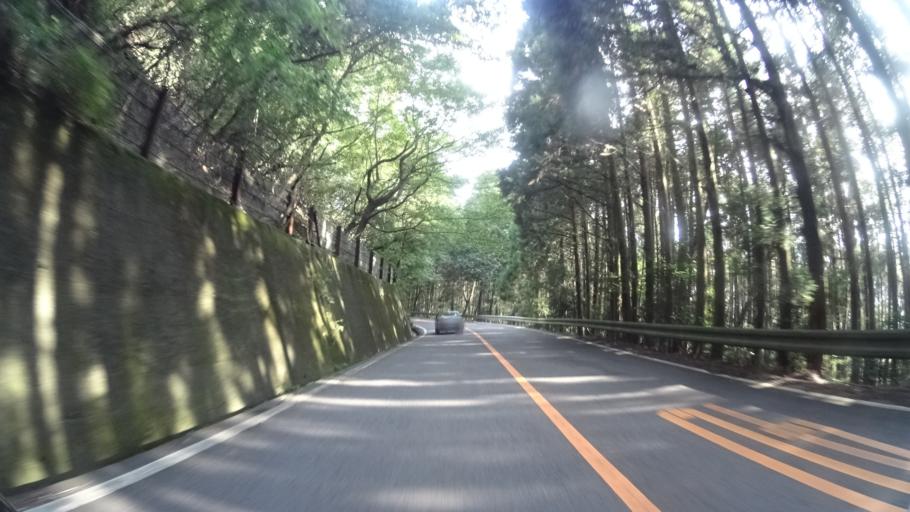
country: JP
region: Oita
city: Beppu
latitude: 33.2659
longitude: 131.3708
